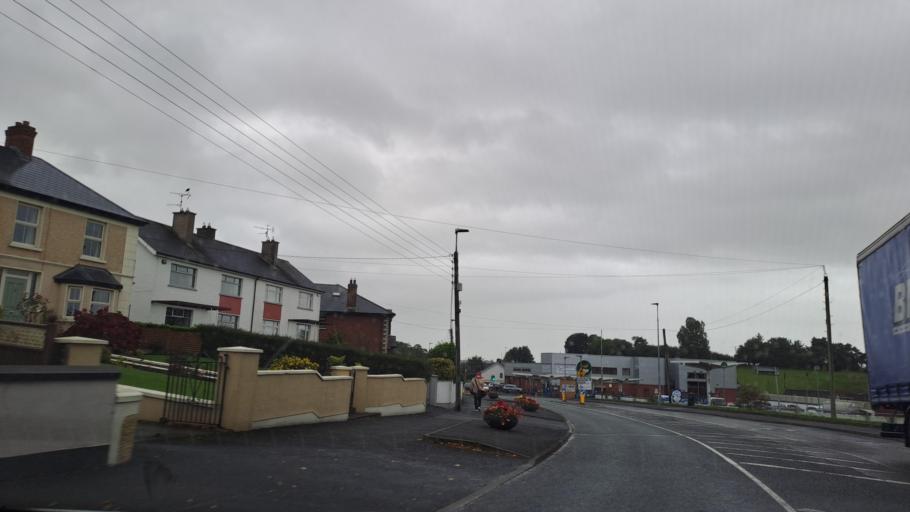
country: IE
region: Ulster
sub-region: County Monaghan
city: Carrickmacross
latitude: 53.9819
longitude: -6.7178
